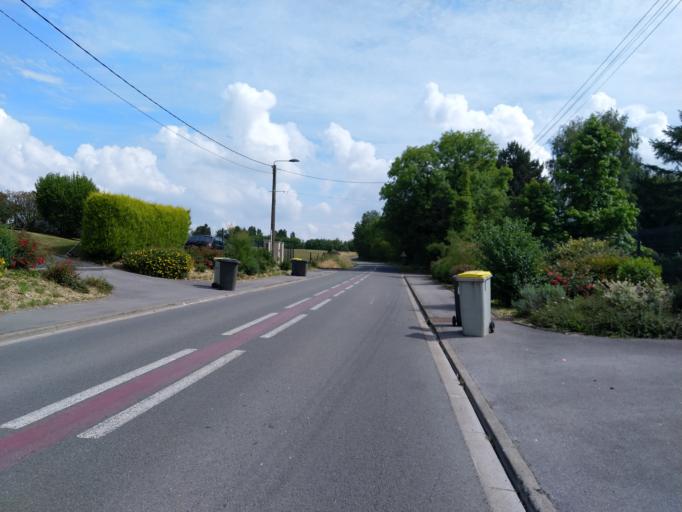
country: FR
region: Nord-Pas-de-Calais
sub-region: Departement du Nord
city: Maubeuge
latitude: 50.2906
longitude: 3.9882
